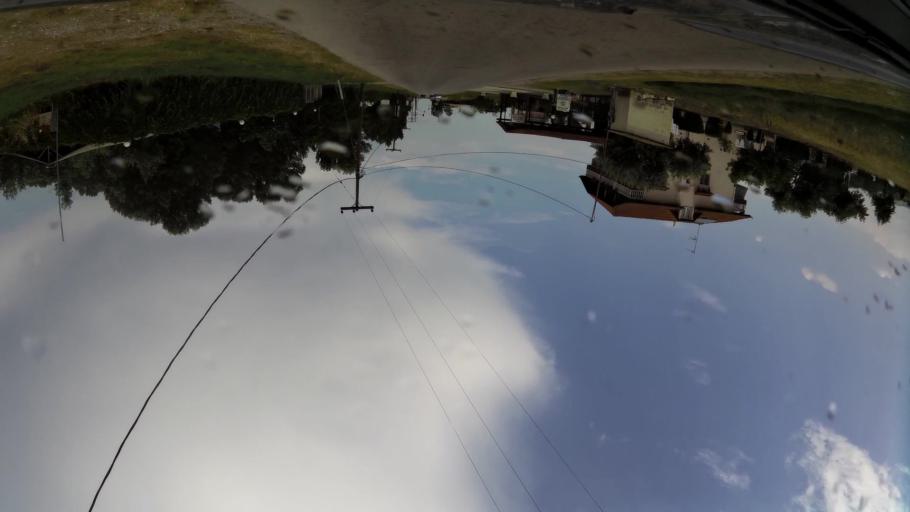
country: GR
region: Central Macedonia
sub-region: Nomos Pierias
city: Korinos
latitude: 40.3050
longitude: 22.6146
